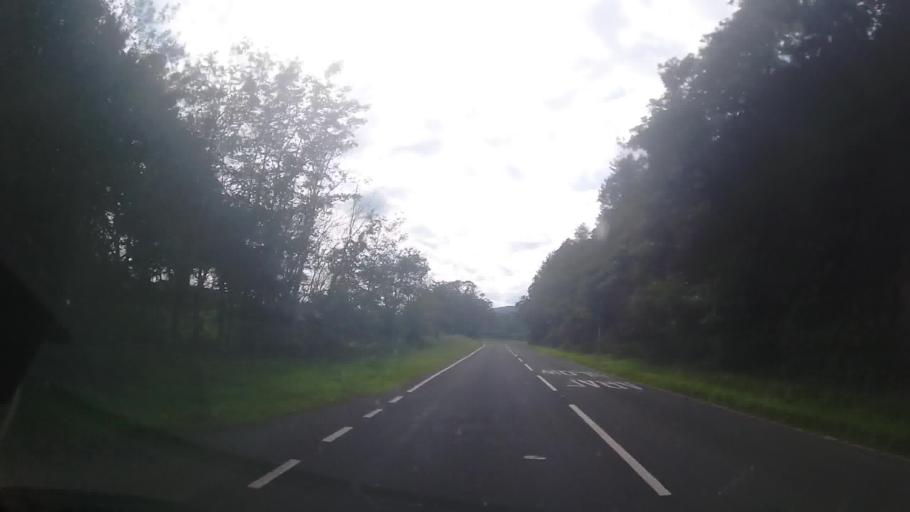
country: GB
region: Wales
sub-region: Gwynedd
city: Barmouth
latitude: 52.7428
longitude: -3.9915
